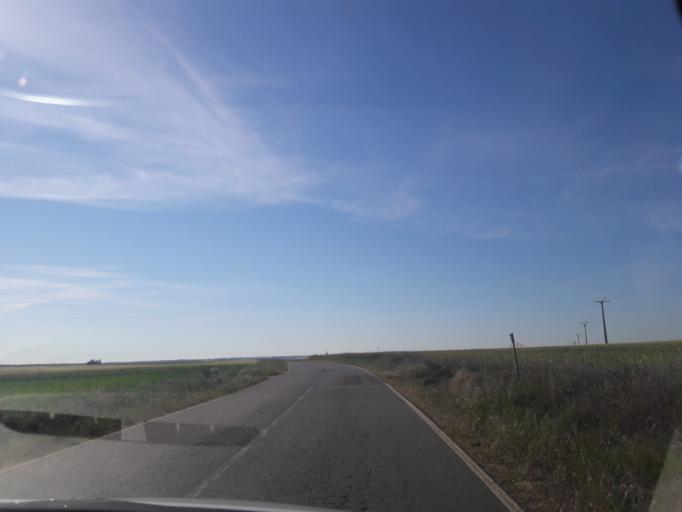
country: ES
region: Castille and Leon
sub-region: Provincia de Salamanca
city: Tardaguila
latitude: 41.1039
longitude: -5.5687
